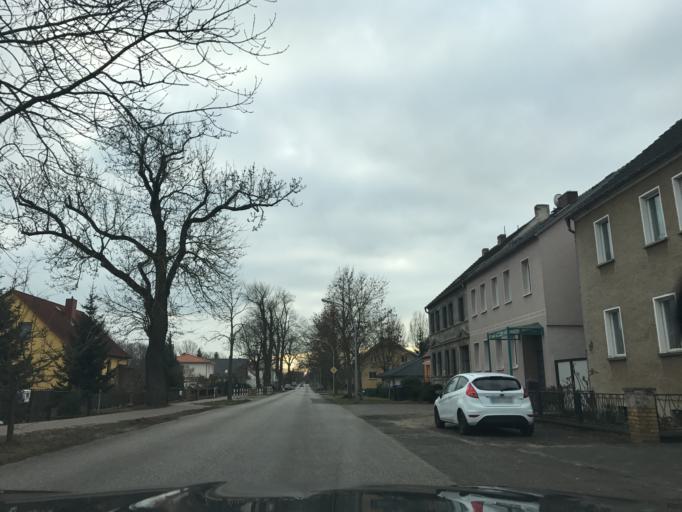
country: DE
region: Brandenburg
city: Brandenburg an der Havel
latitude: 52.3883
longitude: 12.5453
